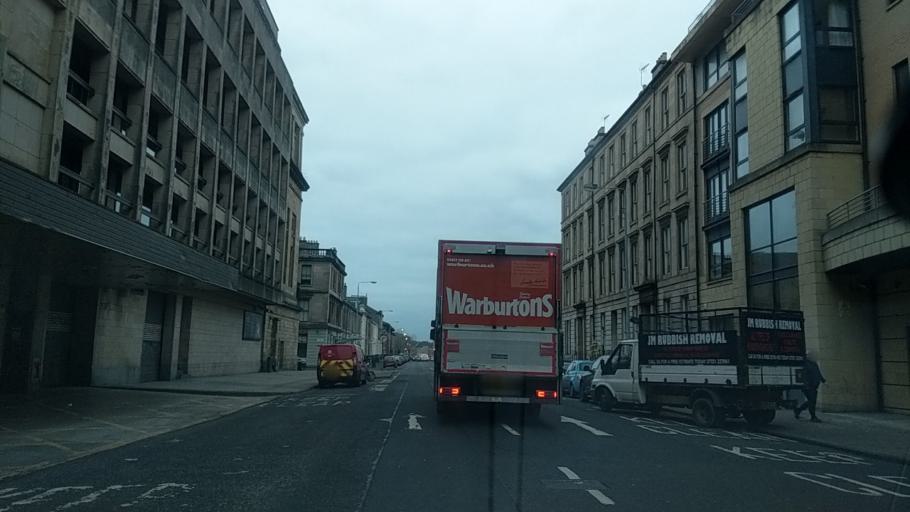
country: GB
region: Scotland
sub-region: Glasgow City
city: Glasgow
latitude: 55.8654
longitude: -4.2724
